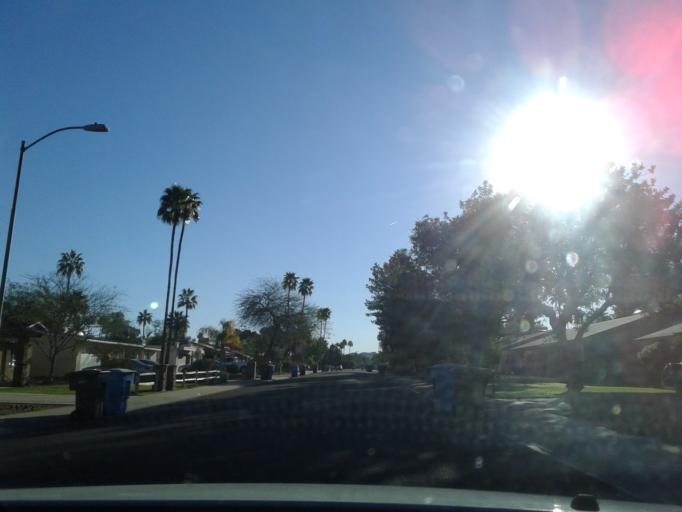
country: US
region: Arizona
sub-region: Maricopa County
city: Glendale
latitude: 33.6108
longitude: -112.0731
